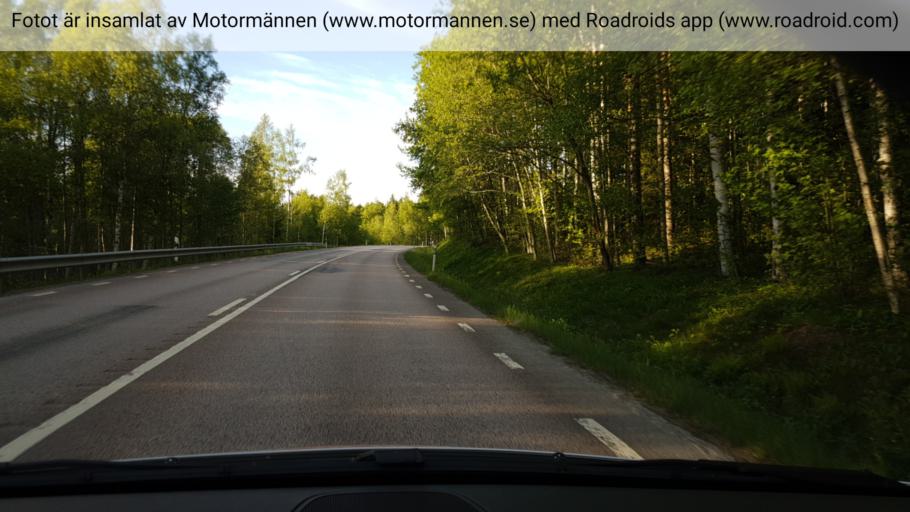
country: SE
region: Vaestmanland
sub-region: Fagersta Kommun
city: Fagersta
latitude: 59.9380
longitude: 15.7318
